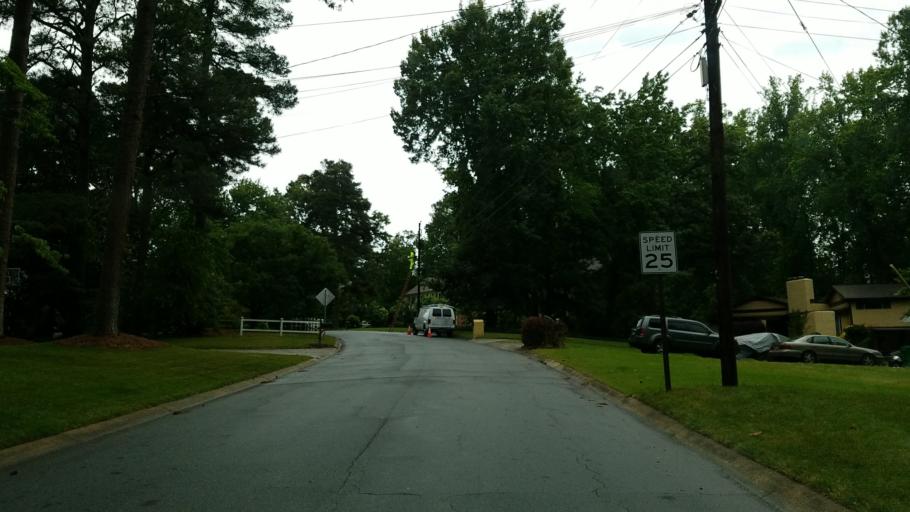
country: US
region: Georgia
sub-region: DeKalb County
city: Dunwoody
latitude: 33.9445
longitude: -84.3428
